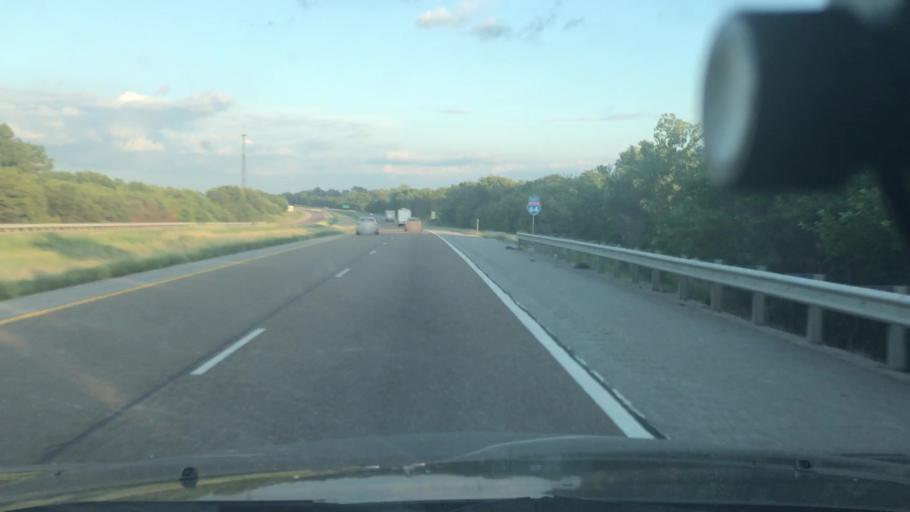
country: US
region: Illinois
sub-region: Clinton County
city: New Baden
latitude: 38.5298
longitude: -89.7244
